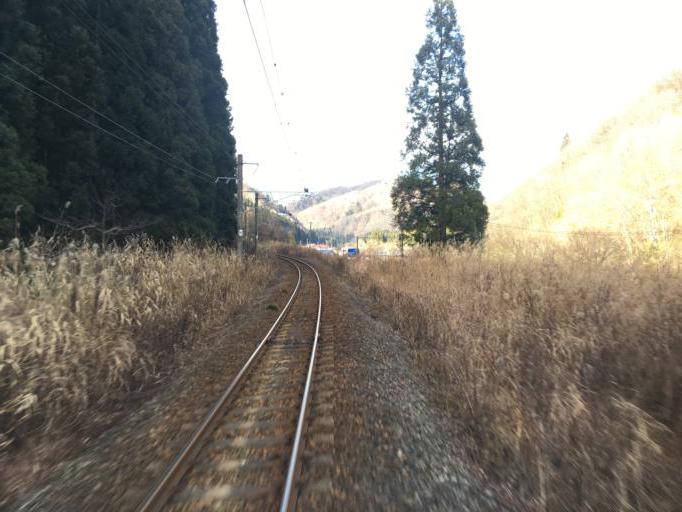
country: JP
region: Akita
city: Yuzawa
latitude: 38.9865
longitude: 140.3625
